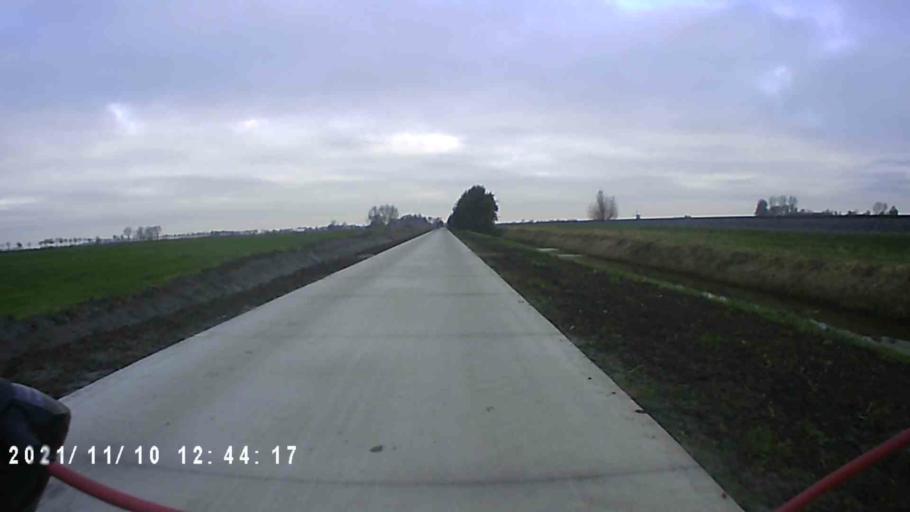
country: NL
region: Groningen
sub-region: Gemeente Groningen
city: Korrewegwijk
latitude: 53.2567
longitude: 6.5497
